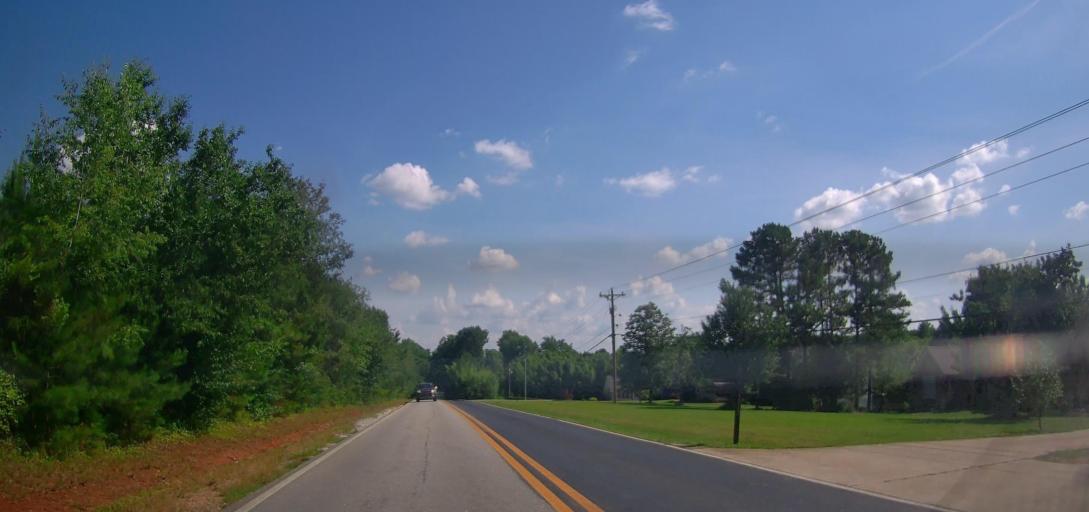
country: US
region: Georgia
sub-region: Spalding County
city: East Griffin
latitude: 33.2893
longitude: -84.1899
